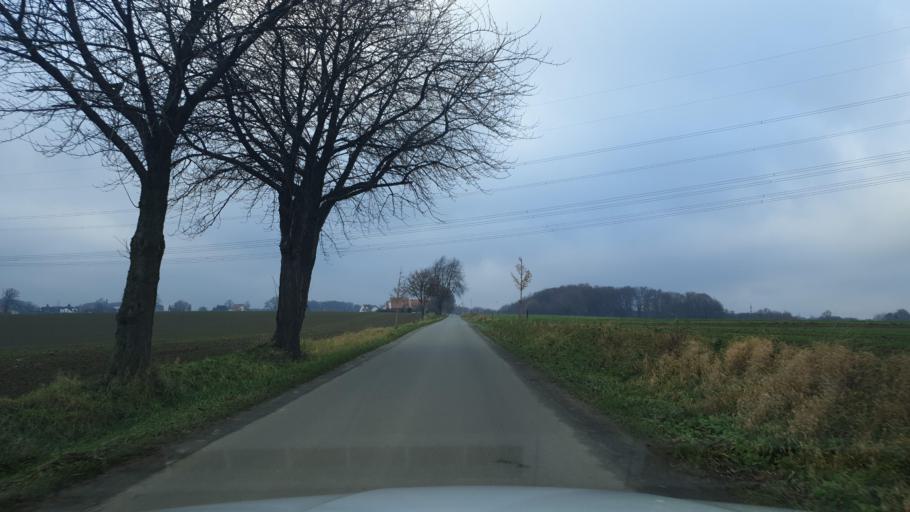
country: DE
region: North Rhine-Westphalia
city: Enger
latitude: 52.1180
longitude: 8.6005
